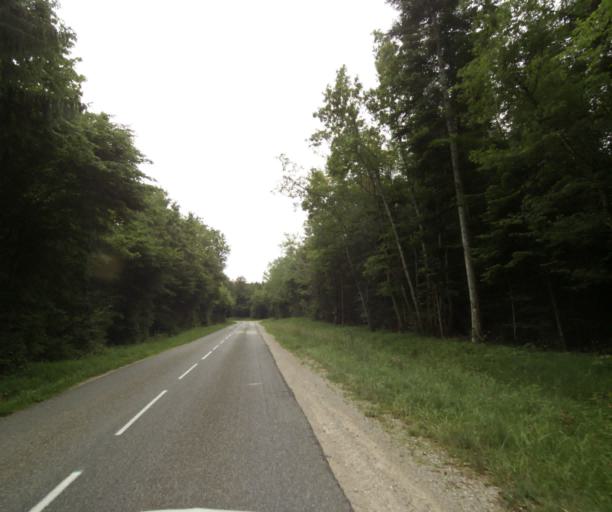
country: FR
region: Rhone-Alpes
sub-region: Departement de la Haute-Savoie
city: Sciez
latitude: 46.3202
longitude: 6.3959
